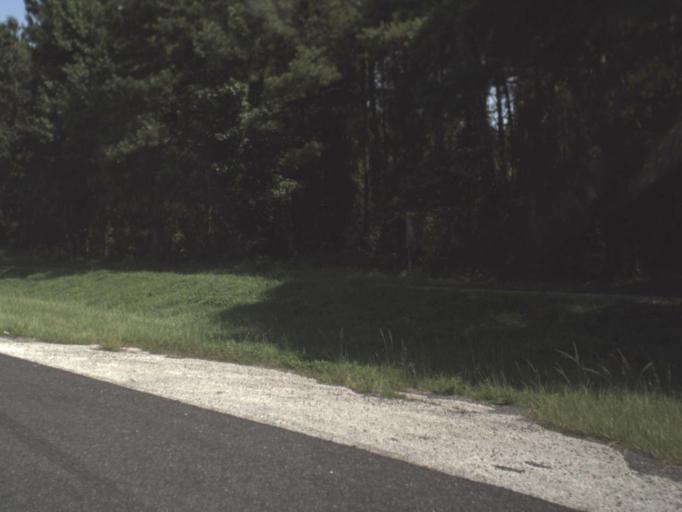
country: US
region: Florida
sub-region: Hernando County
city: Brooksville
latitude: 28.5410
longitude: -82.3630
